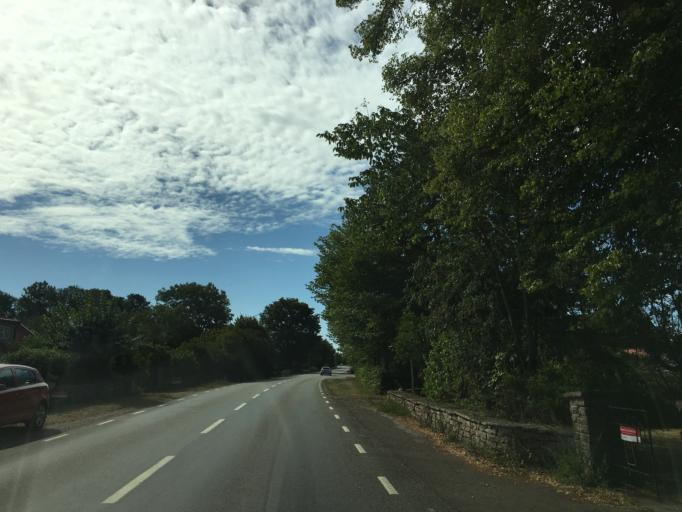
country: SE
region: Kalmar
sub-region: Morbylanga Kommun
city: Moerbylanga
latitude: 56.4558
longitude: 16.4297
